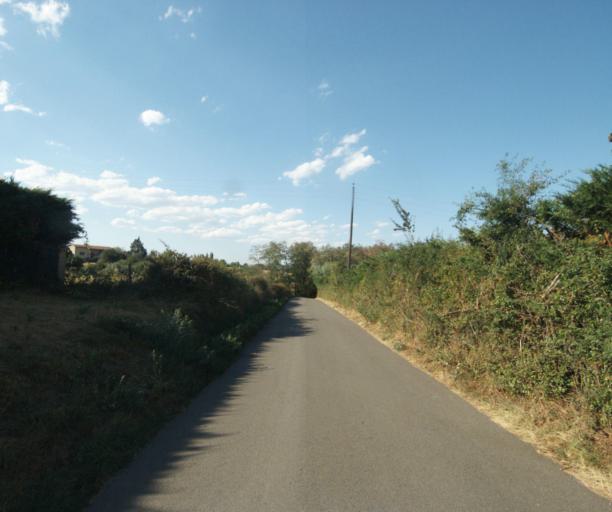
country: FR
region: Rhone-Alpes
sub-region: Departement du Rhone
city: Sainte-Consorce
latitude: 45.7950
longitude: 4.6901
